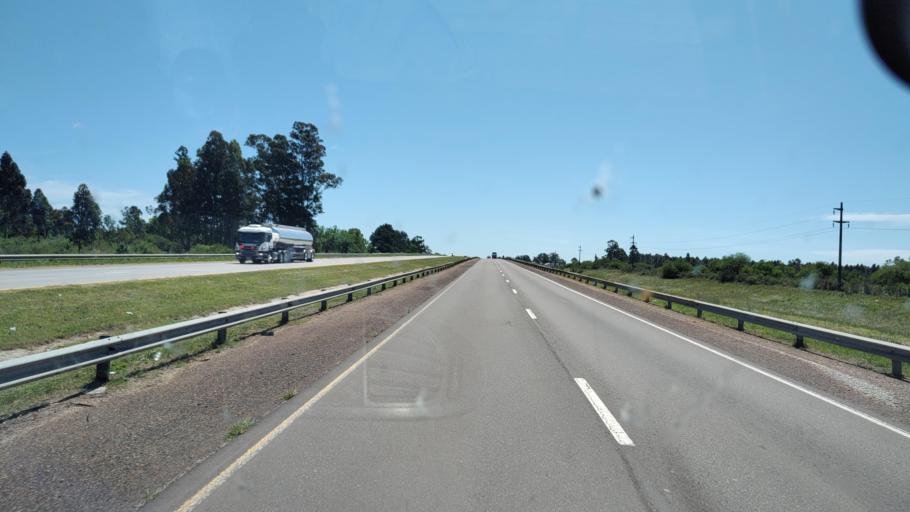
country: AR
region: Entre Rios
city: Colon
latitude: -32.1879
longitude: -58.2387
